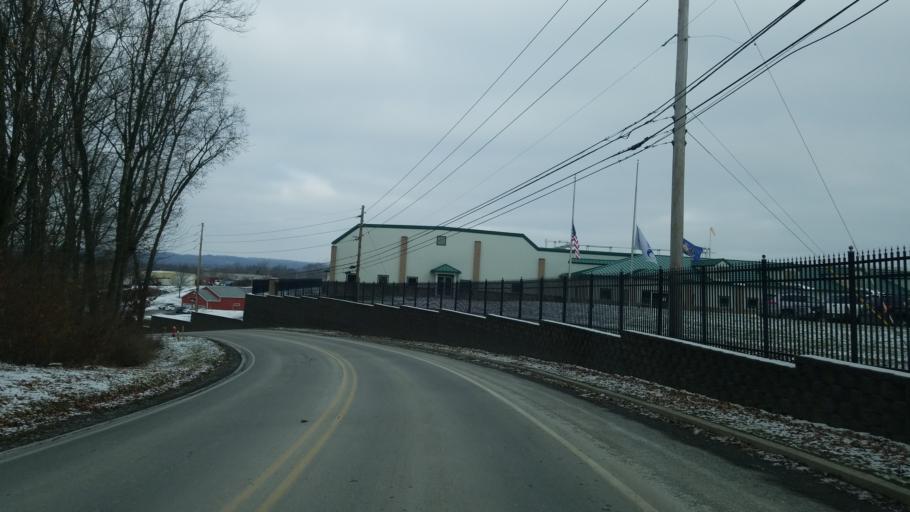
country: US
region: Pennsylvania
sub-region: Clearfield County
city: DuBois
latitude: 41.1055
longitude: -78.7325
